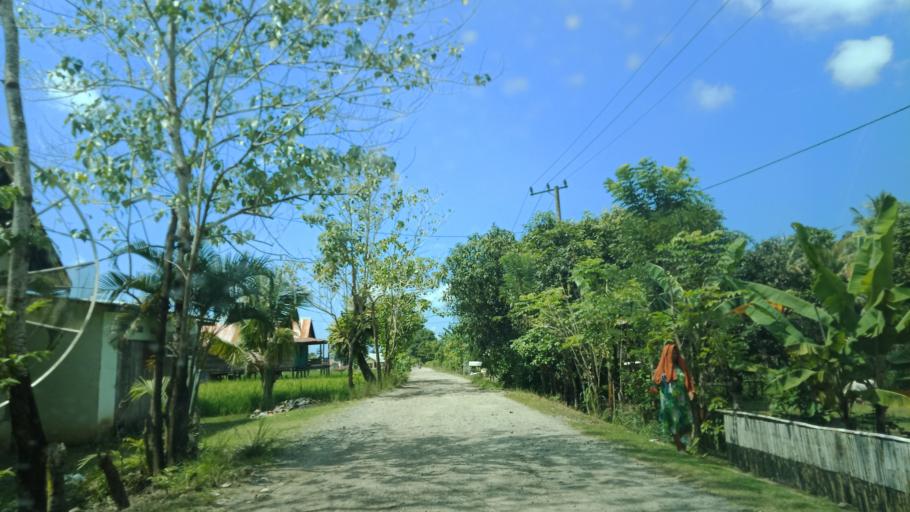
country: ID
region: South Sulawesi
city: Kadai
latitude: -4.7740
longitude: 120.3392
